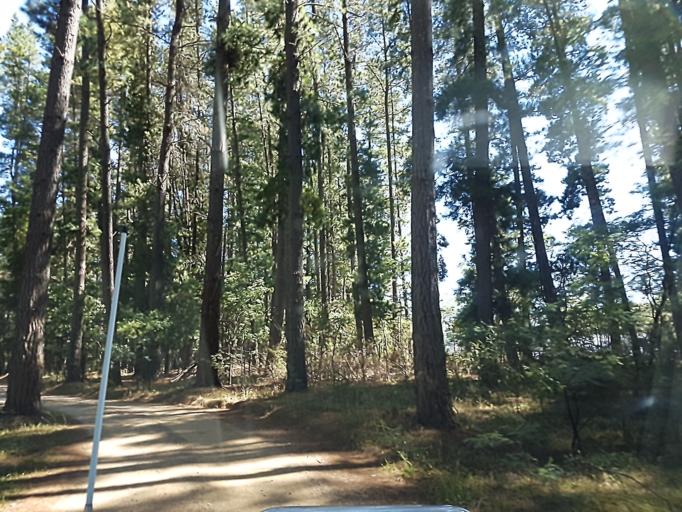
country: AU
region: Victoria
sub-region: Alpine
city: Mount Beauty
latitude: -36.8945
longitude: 147.0680
